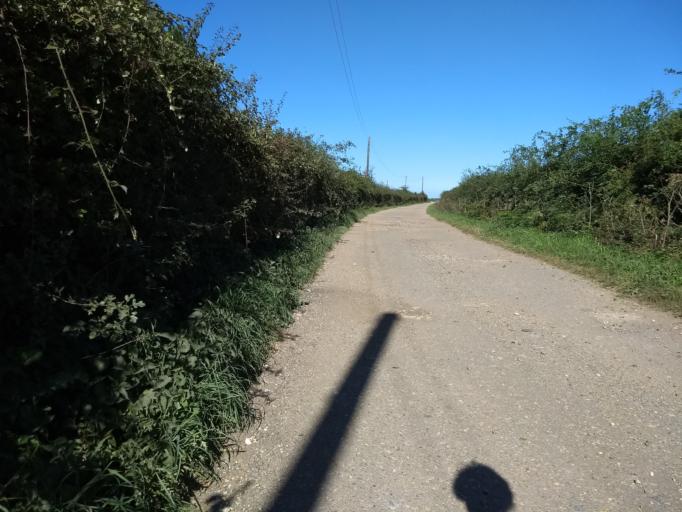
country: GB
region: England
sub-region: Isle of Wight
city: Niton
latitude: 50.6256
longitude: -1.2900
